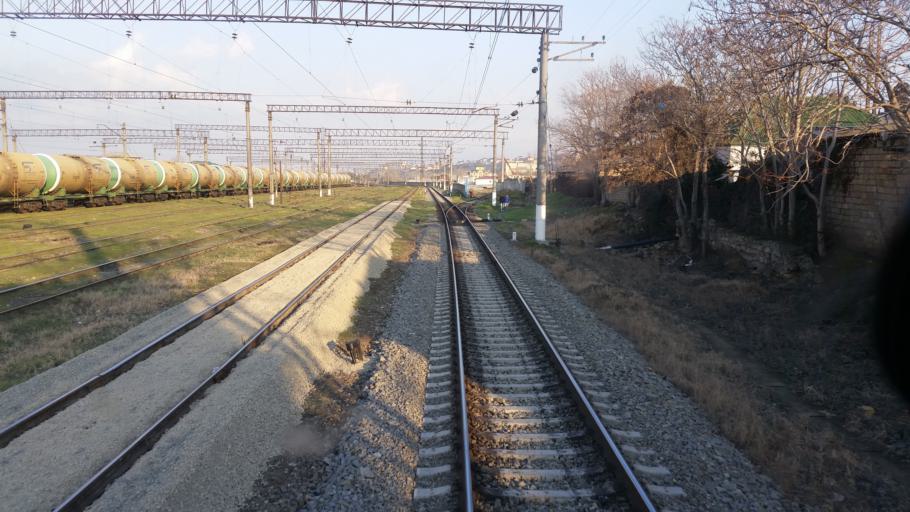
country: AZ
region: Baki
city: Bilajari
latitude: 40.4333
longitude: 49.8092
